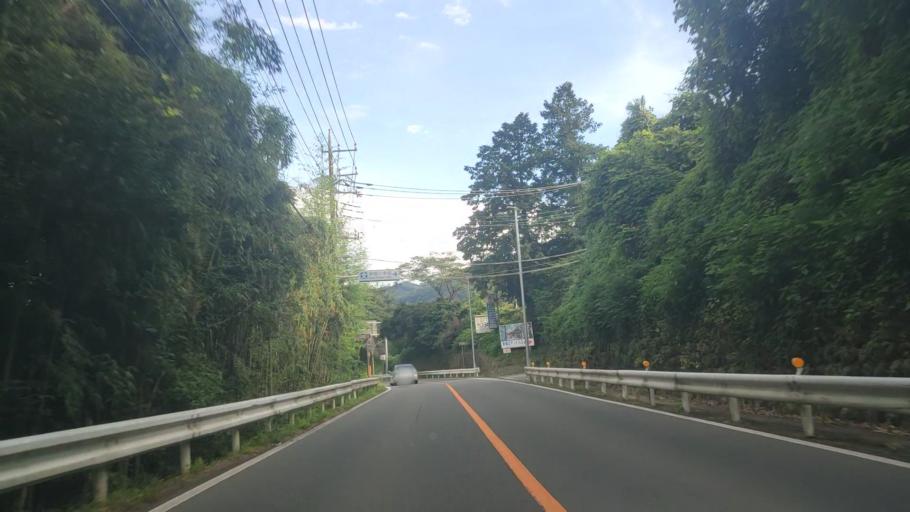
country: JP
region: Gunma
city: Omamacho-omama
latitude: 36.4687
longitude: 139.2575
